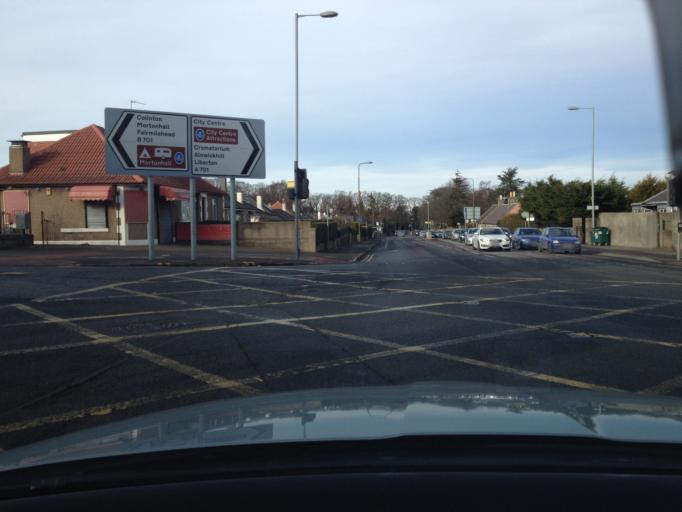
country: GB
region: Scotland
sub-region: Midlothian
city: Loanhead
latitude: 55.9001
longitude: -3.1629
